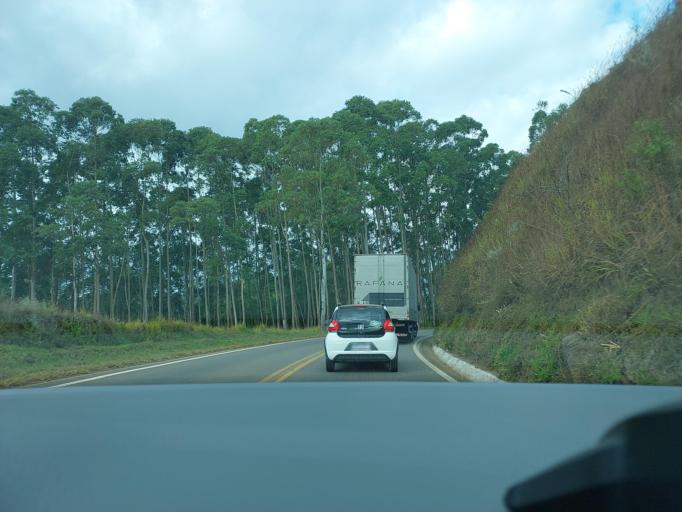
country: BR
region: Minas Gerais
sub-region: Visconde Do Rio Branco
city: Visconde do Rio Branco
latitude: -20.9504
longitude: -42.6113
